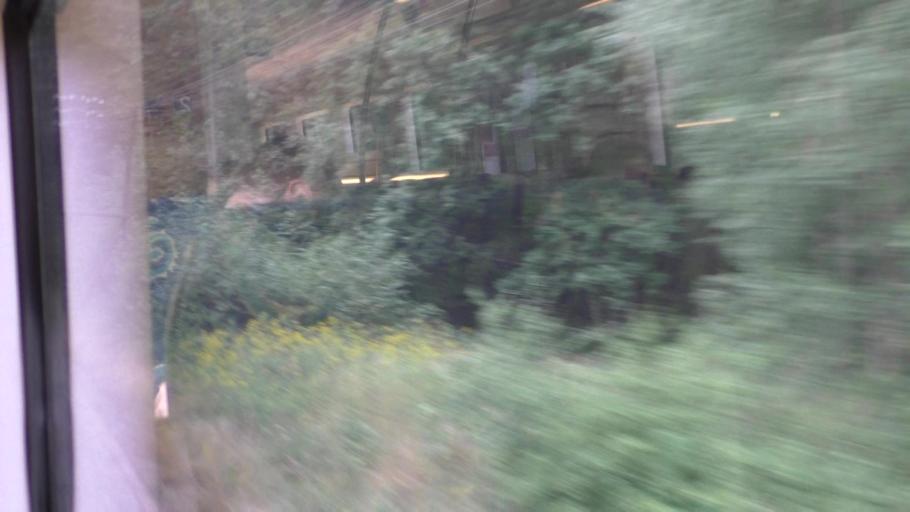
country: DE
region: Saxony
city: Horka
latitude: 51.2764
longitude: 14.9039
